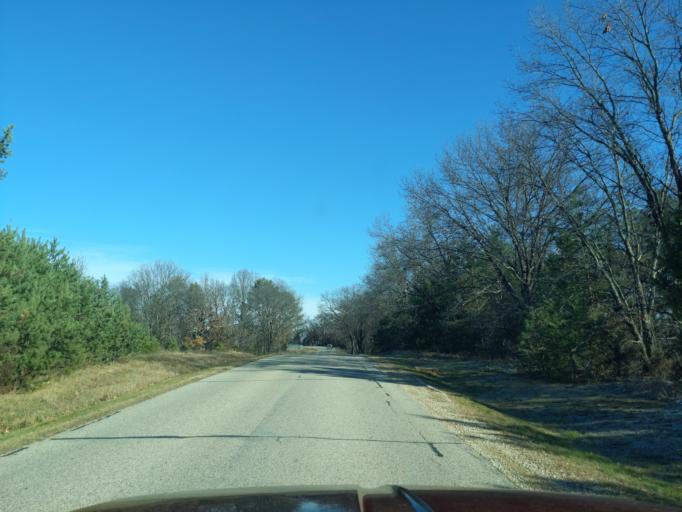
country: US
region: Wisconsin
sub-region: Waushara County
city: Silver Lake
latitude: 44.0895
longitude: -89.1909
